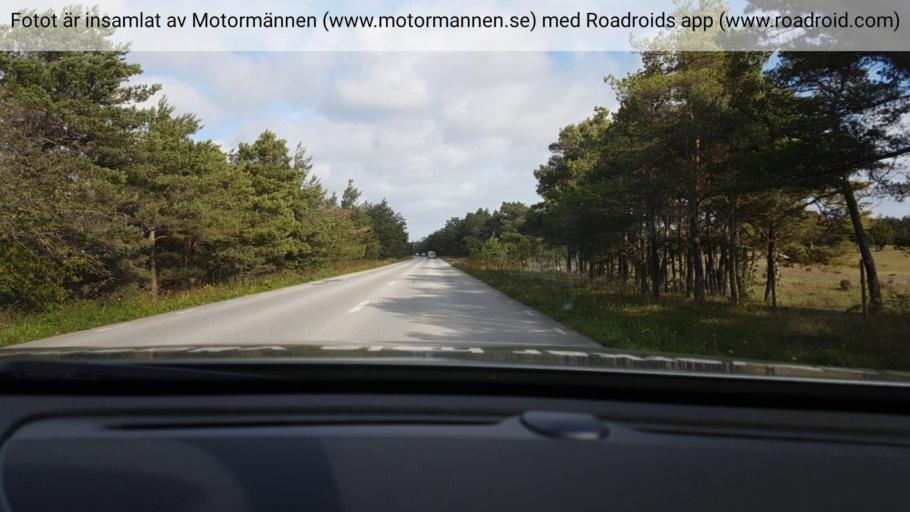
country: SE
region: Gotland
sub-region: Gotland
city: Slite
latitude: 57.8805
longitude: 19.0874
